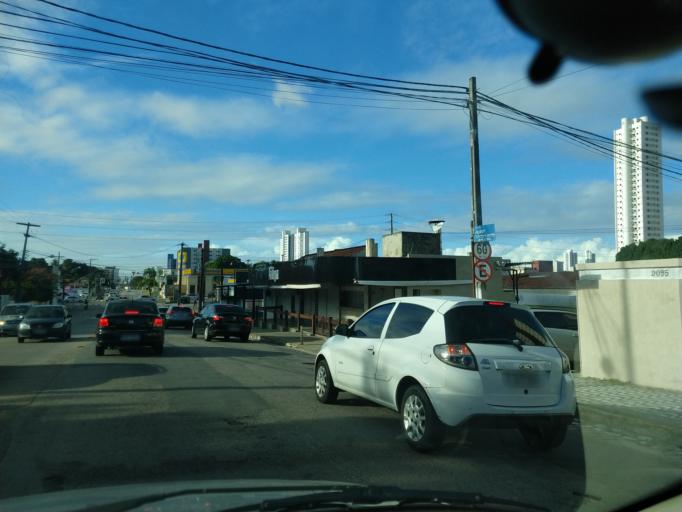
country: BR
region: Rio Grande do Norte
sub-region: Natal
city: Natal
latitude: -5.8184
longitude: -35.2182
